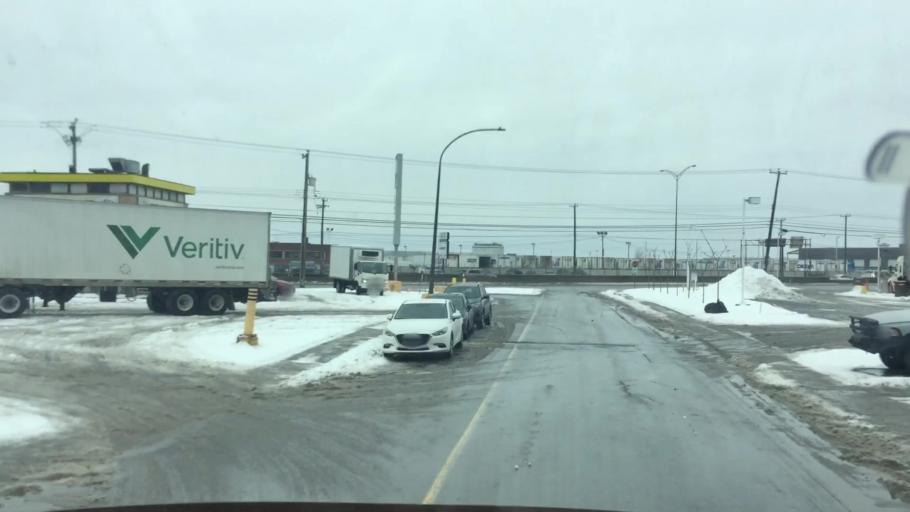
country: CA
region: Quebec
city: Dorval
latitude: 45.4616
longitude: -73.7221
